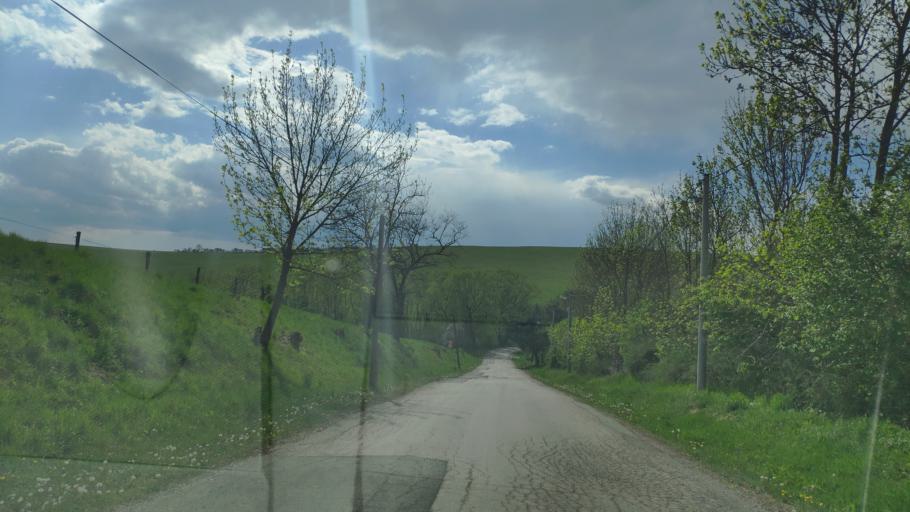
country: SK
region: Kosicky
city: Moldava nad Bodvou
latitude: 48.5855
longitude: 20.9176
